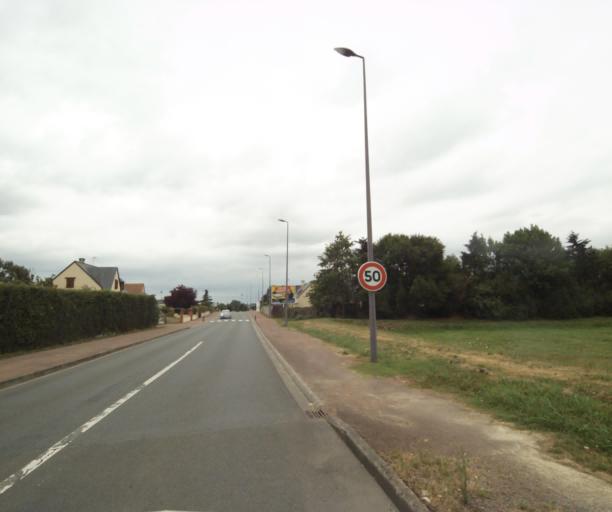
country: FR
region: Pays de la Loire
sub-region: Departement de la Sarthe
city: Sable-sur-Sarthe
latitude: 47.8266
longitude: -0.3191
